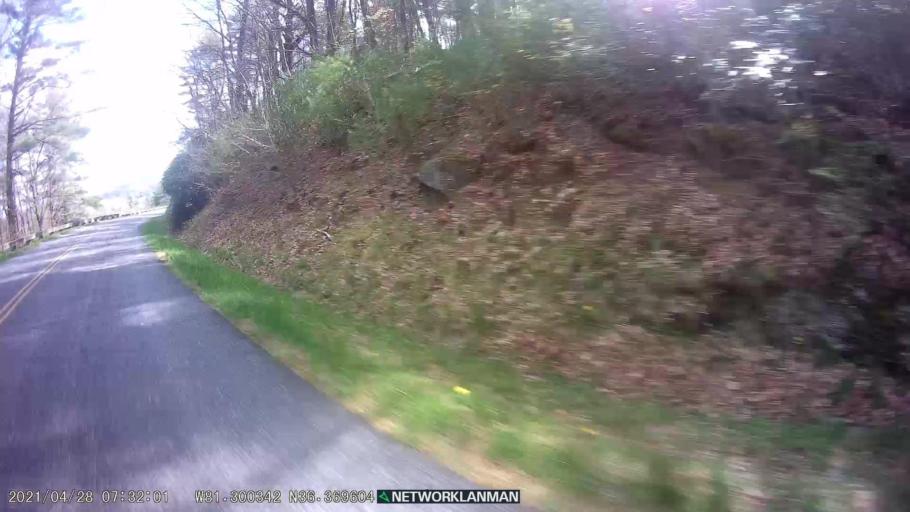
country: US
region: North Carolina
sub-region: Wilkes County
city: Mulberry
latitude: 36.3698
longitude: -81.3005
